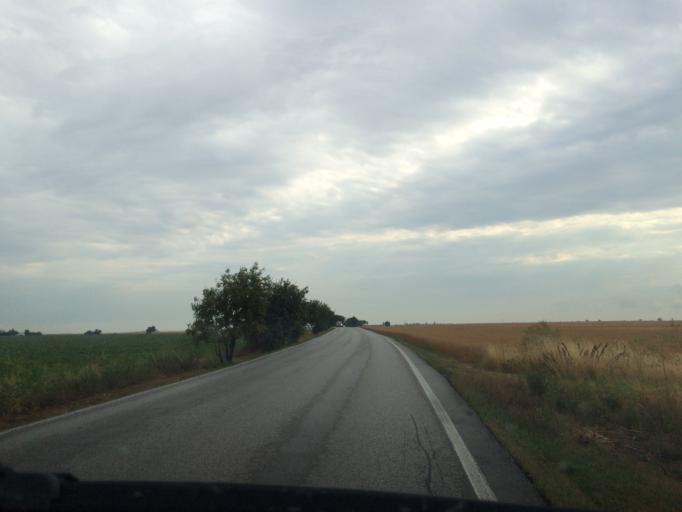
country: CZ
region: Central Bohemia
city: Horomerice
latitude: 50.1164
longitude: 14.3137
